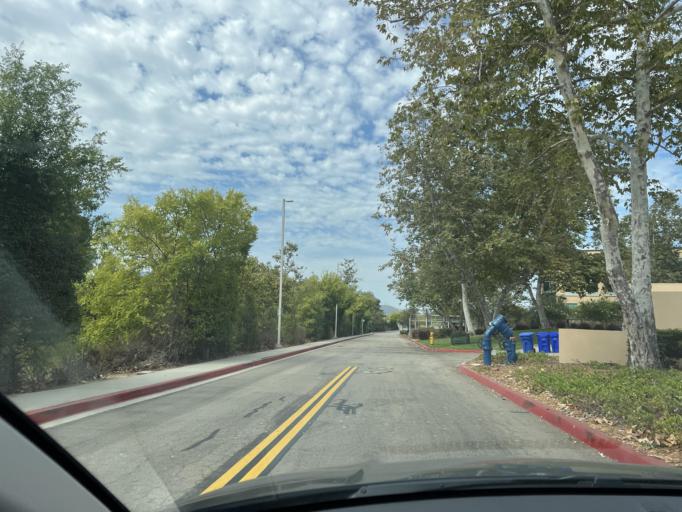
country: US
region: California
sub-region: San Diego County
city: San Marcos
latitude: 33.1405
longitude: -117.1593
